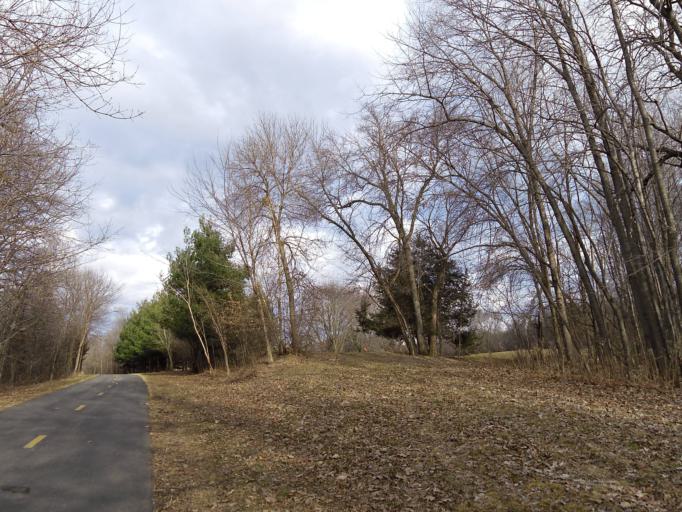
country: US
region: Minnesota
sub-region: Scott County
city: Prior Lake
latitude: 44.6909
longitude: -93.3842
